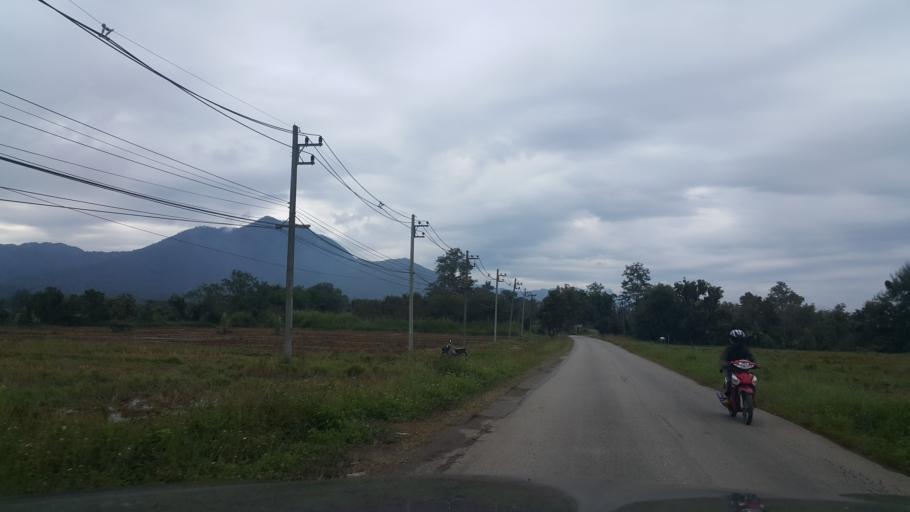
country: TH
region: Chiang Mai
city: Mae On
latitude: 18.7659
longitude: 99.2504
